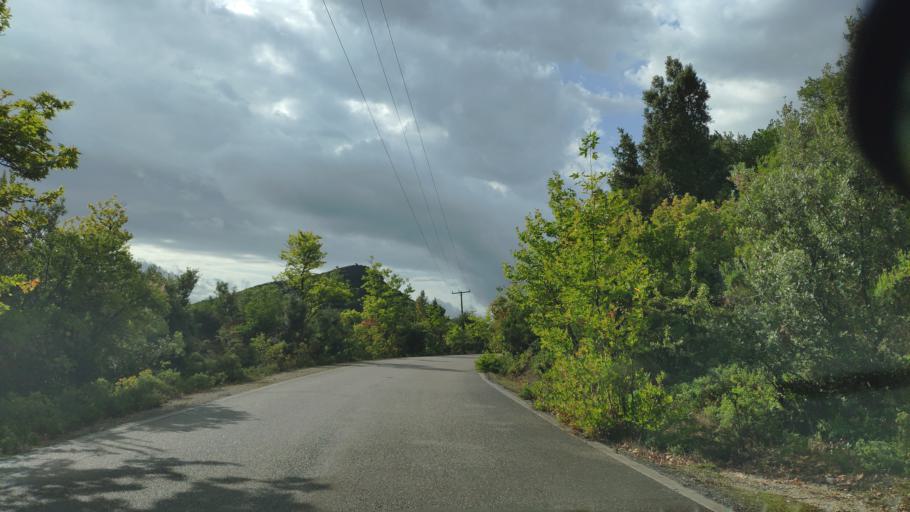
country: GR
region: West Greece
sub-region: Nomos Aitolias kai Akarnanias
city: Sardinia
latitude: 38.8586
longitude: 21.3061
